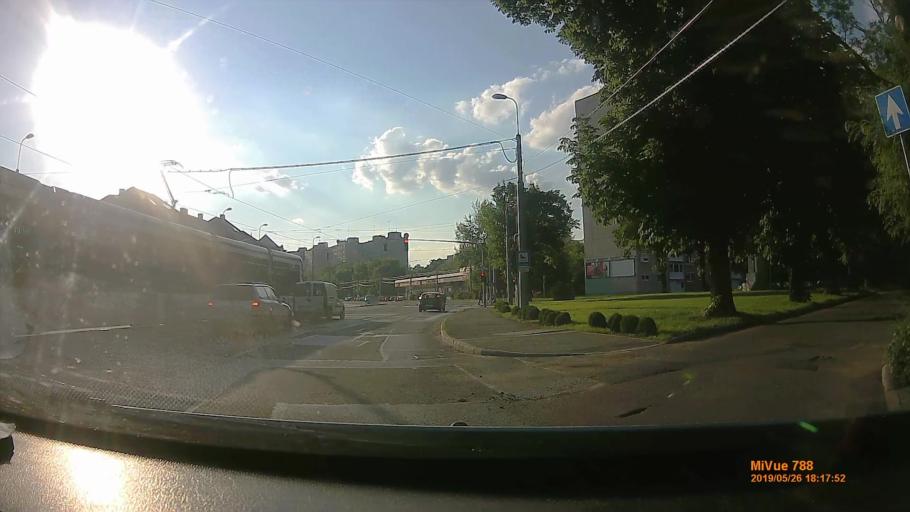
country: HU
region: Borsod-Abauj-Zemplen
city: Sajobabony
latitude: 48.1002
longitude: 20.6925
